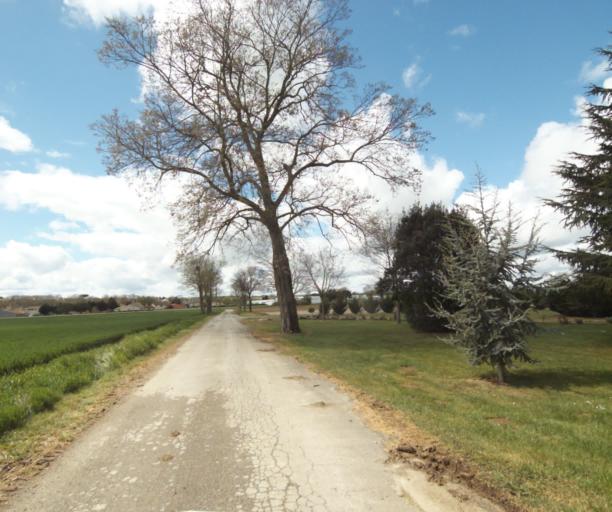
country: FR
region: Midi-Pyrenees
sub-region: Departement de l'Ariege
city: Saverdun
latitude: 43.2471
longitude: 1.5755
